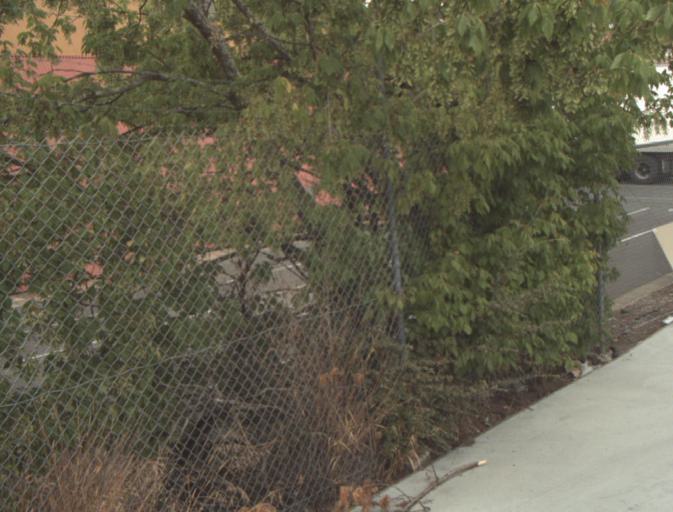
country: AU
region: Tasmania
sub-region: Launceston
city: West Launceston
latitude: -41.4508
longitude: 147.1443
